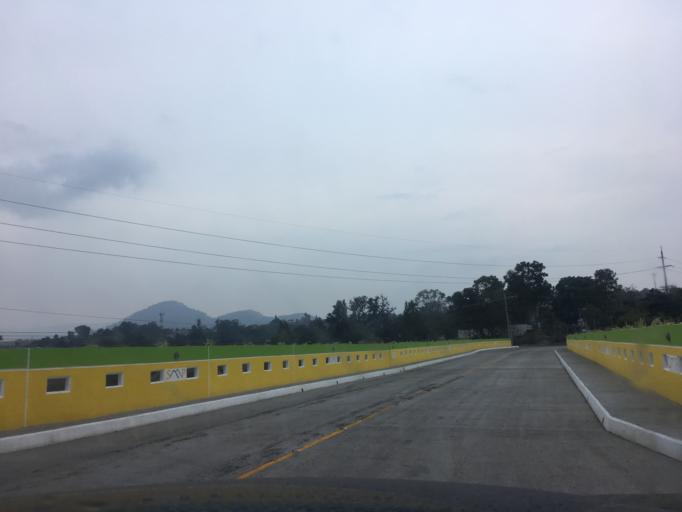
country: GT
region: Guatemala
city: Petapa
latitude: 14.5133
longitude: -90.5531
